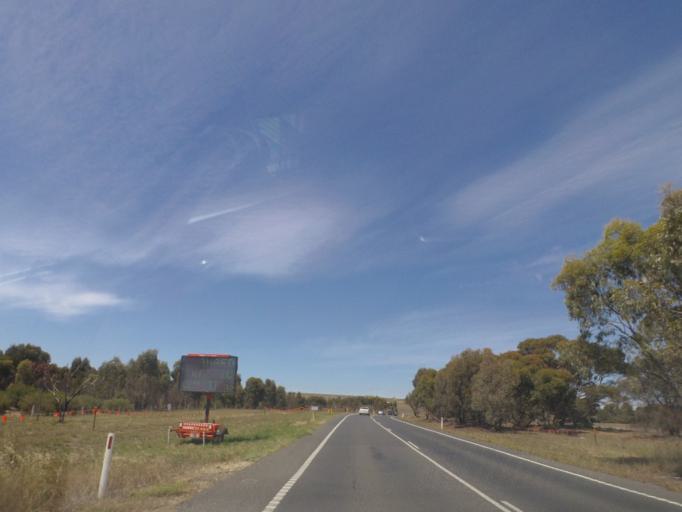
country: AU
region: Victoria
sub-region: Greater Geelong
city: Lara
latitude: -37.8833
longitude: 144.3783
